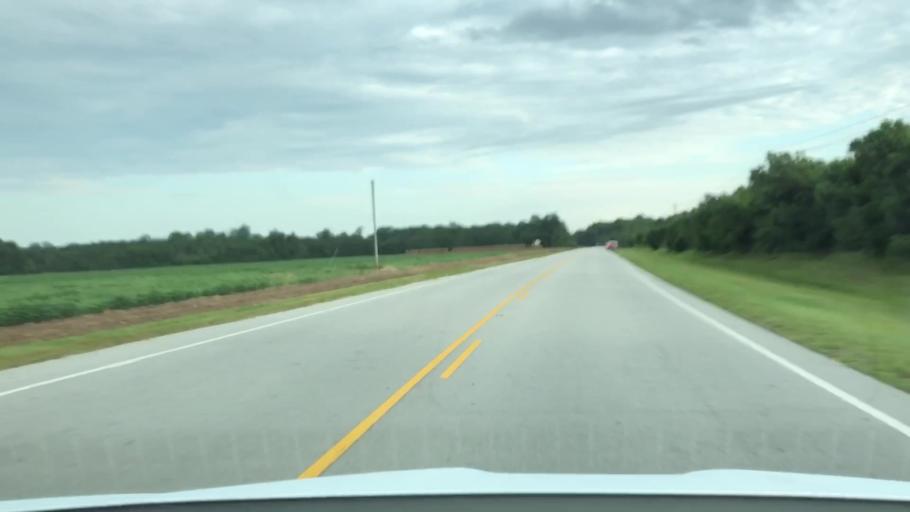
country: US
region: North Carolina
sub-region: Jones County
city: Trenton
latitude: 35.0018
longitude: -77.2749
